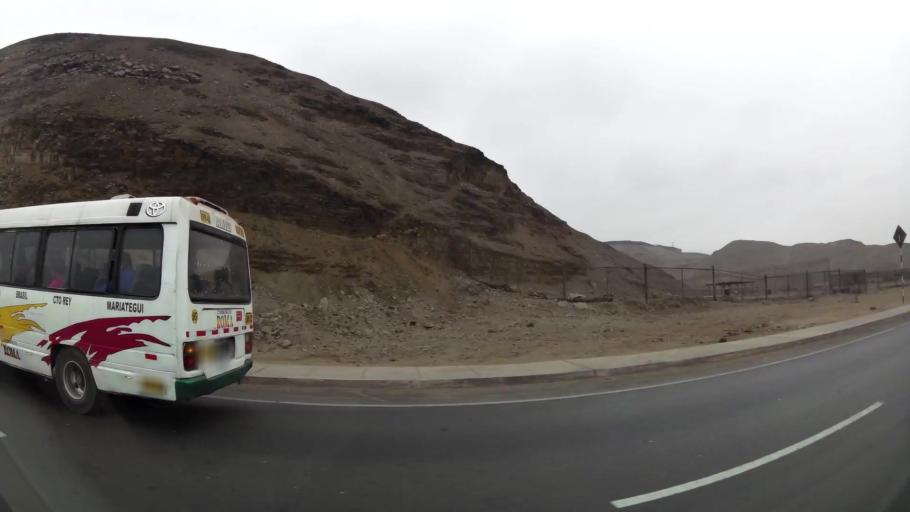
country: PE
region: Lima
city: Ventanilla
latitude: -11.9283
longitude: -77.1300
